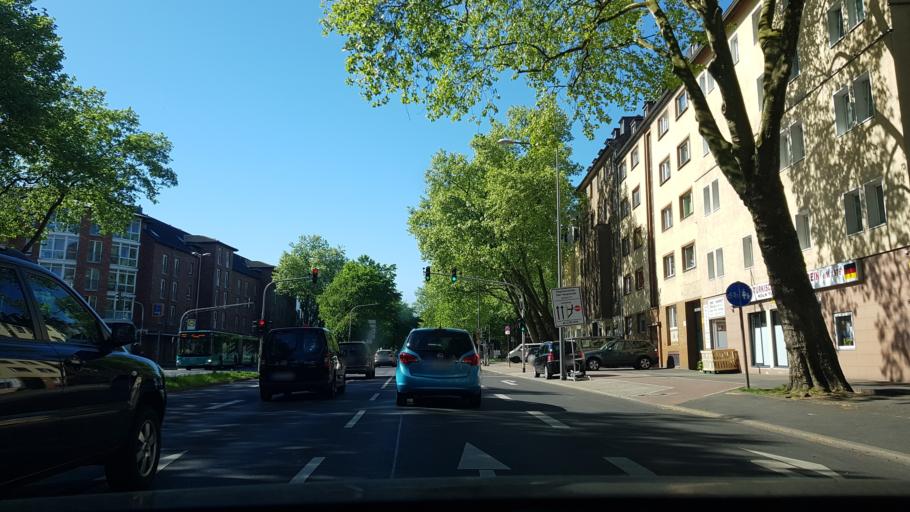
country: DE
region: North Rhine-Westphalia
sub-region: Regierungsbezirk Koln
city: Muelheim
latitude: 50.9687
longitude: 7.0066
